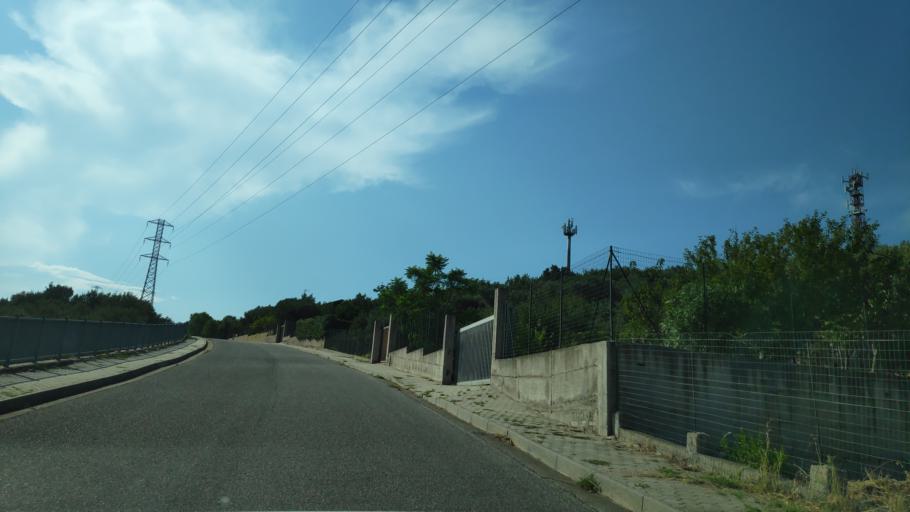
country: IT
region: Calabria
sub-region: Provincia di Catanzaro
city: Martelli-Laganosa
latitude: 38.6852
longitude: 16.5405
